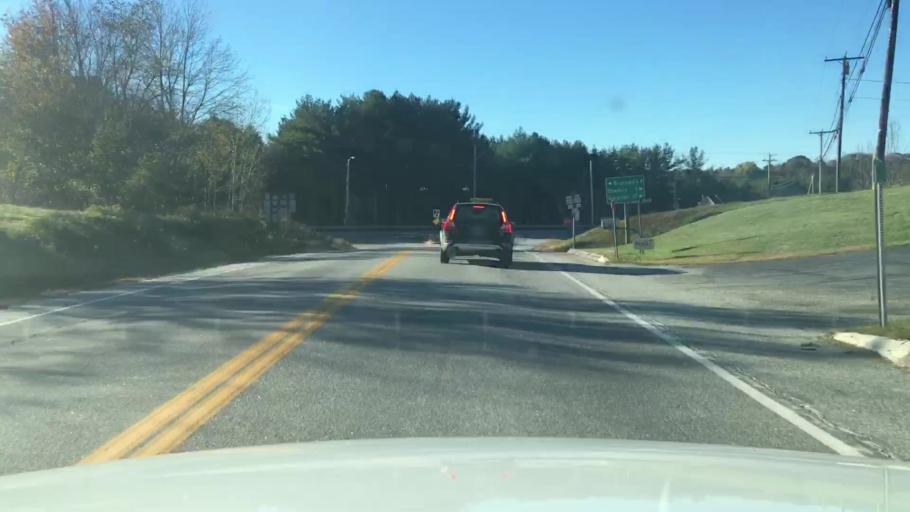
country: US
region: Maine
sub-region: Sagadahoc County
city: Topsham
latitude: 44.0300
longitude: -69.9415
